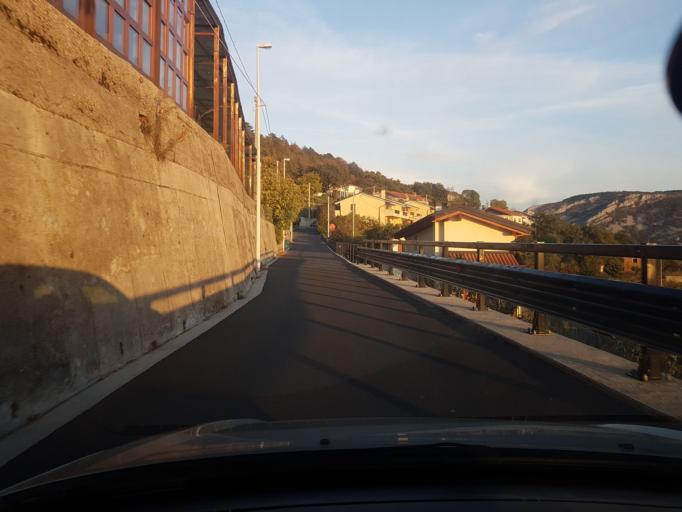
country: IT
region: Friuli Venezia Giulia
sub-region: Provincia di Trieste
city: Domio
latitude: 45.6258
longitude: 13.8429
